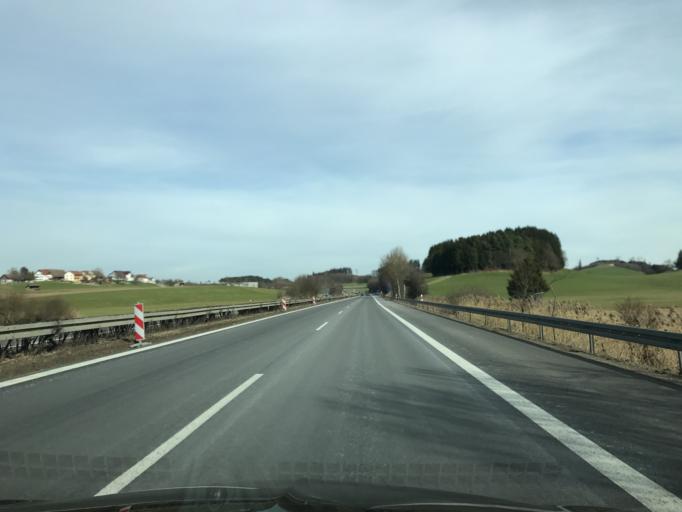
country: DE
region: Bavaria
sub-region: Swabia
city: Weissensberg
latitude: 47.6188
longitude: 9.7369
